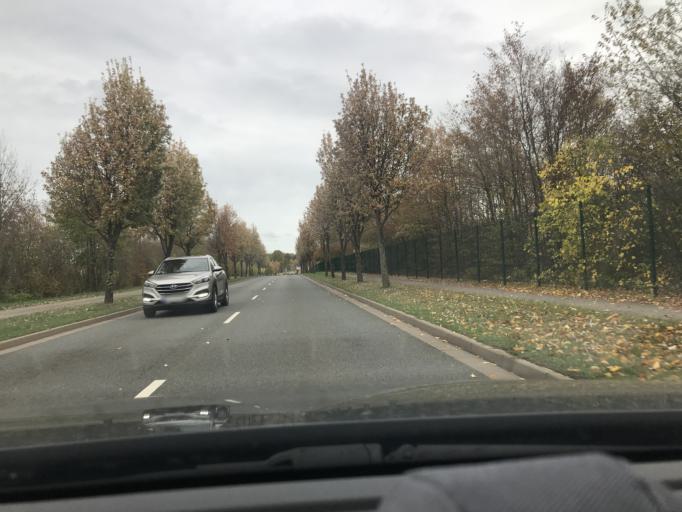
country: DE
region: Thuringia
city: Arnstadt
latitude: 50.8527
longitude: 10.9515
